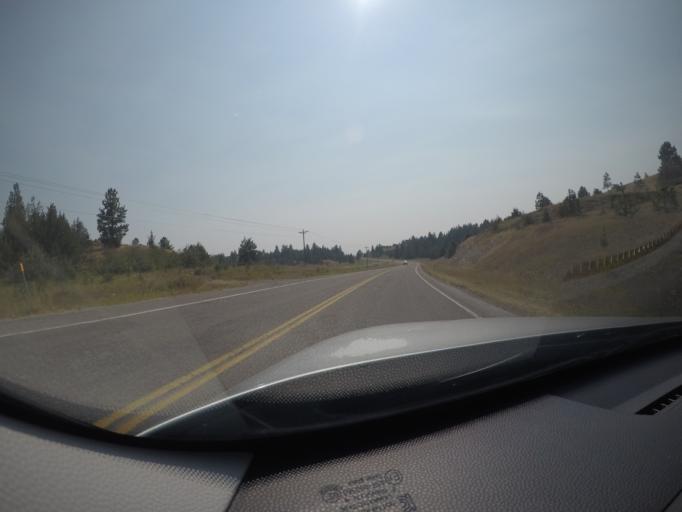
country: US
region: Montana
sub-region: Lake County
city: Polson
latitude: 47.7499
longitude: -114.1696
